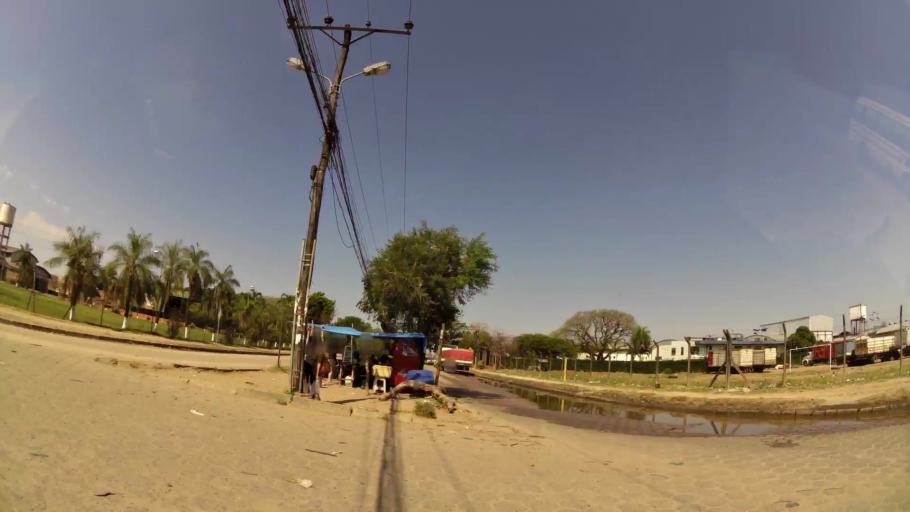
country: BO
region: Santa Cruz
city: Santa Cruz de la Sierra
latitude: -17.7599
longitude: -63.1391
